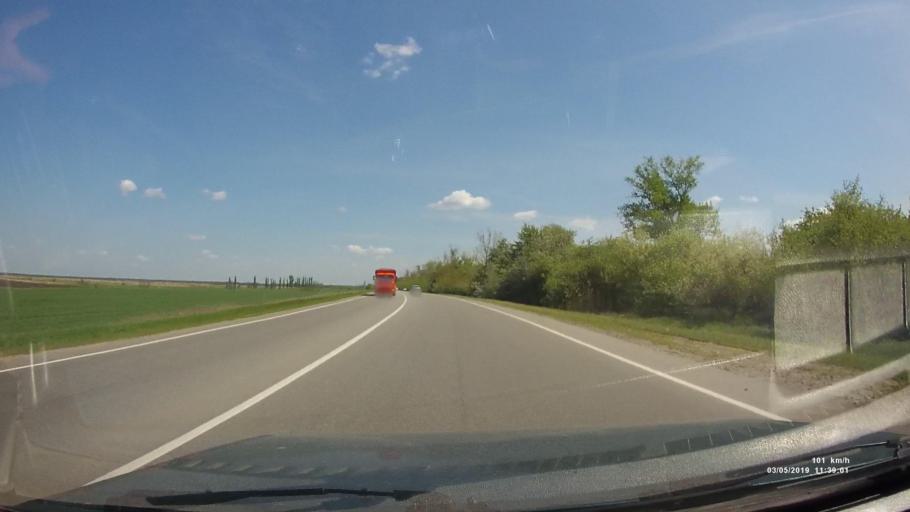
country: RU
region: Rostov
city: Ol'ginskaya
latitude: 47.1312
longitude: 39.9780
